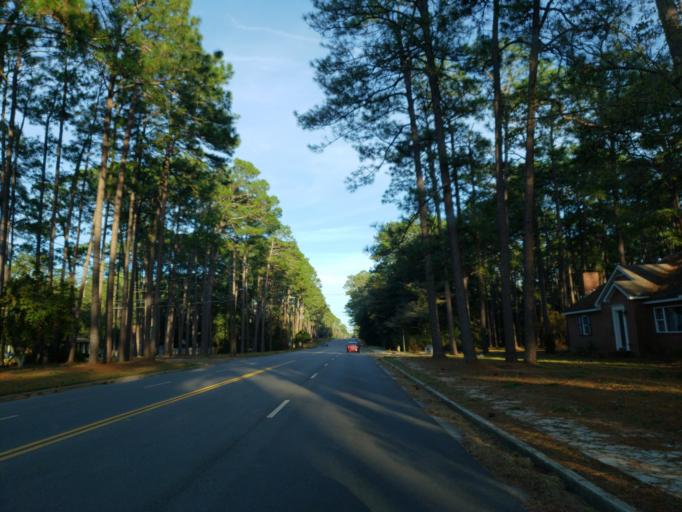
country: US
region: Georgia
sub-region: Tift County
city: Tifton
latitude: 31.4729
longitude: -83.5162
